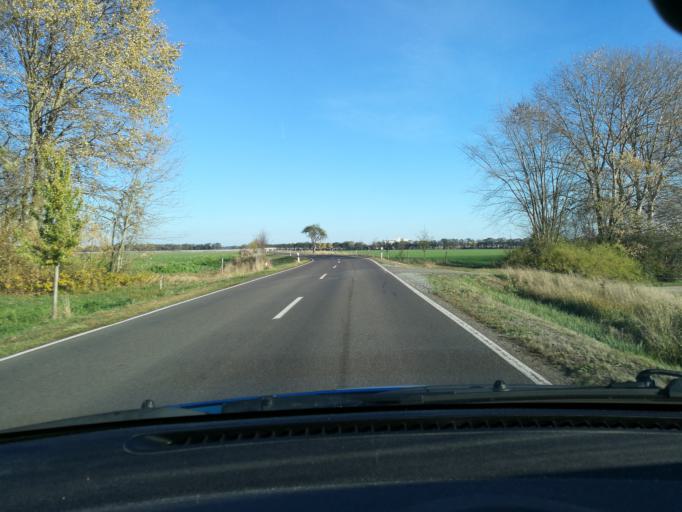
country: DE
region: Brandenburg
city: Karstadt
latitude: 53.1655
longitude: 11.6955
